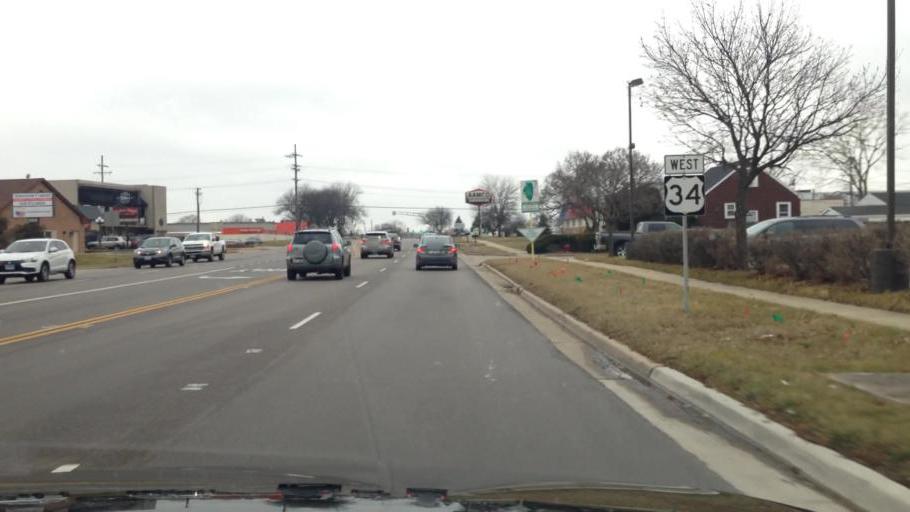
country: US
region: Illinois
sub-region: DuPage County
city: Lisle
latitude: 41.7996
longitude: -88.0913
